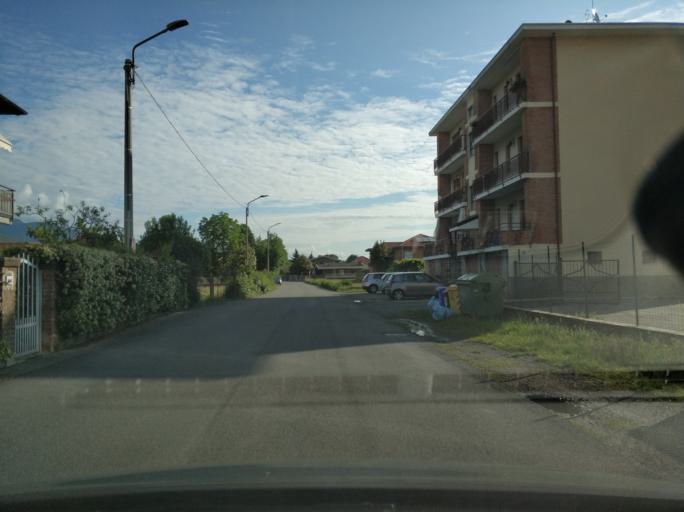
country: IT
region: Piedmont
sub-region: Provincia di Torino
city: Mathi
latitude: 45.2546
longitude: 7.5358
